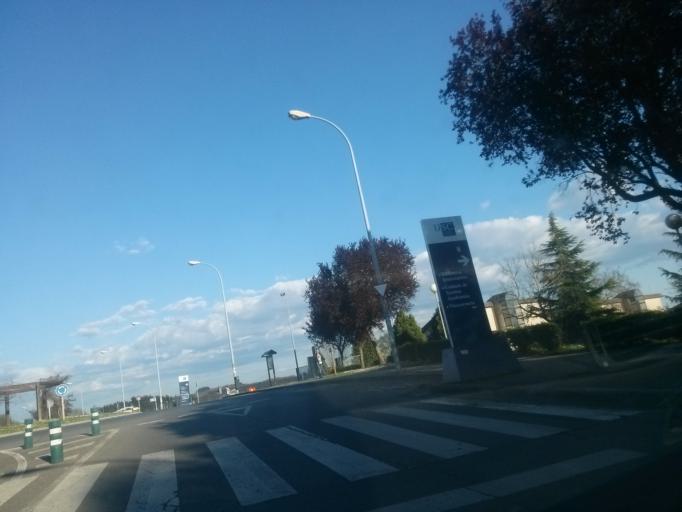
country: ES
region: Galicia
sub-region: Provincia de Lugo
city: Lugo
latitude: 42.9949
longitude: -7.5466
